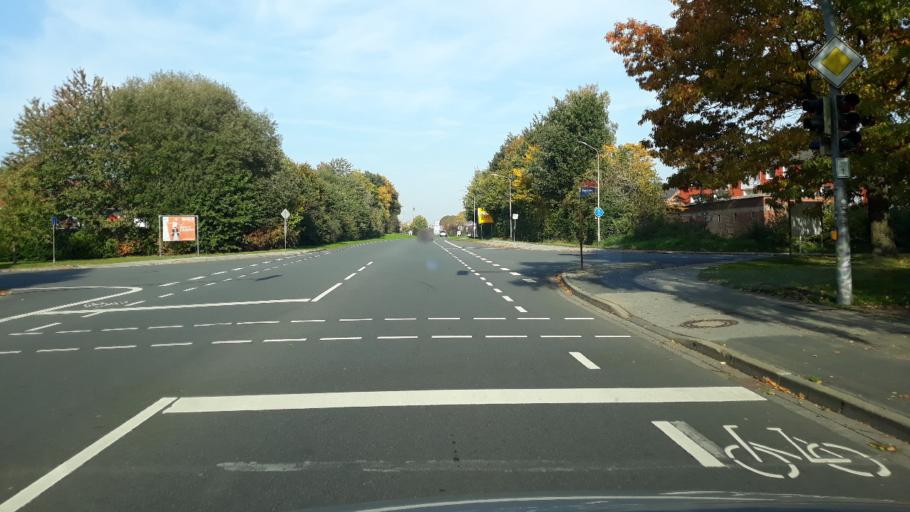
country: DE
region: Schleswig-Holstein
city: Schleswig
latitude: 54.5284
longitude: 9.5717
